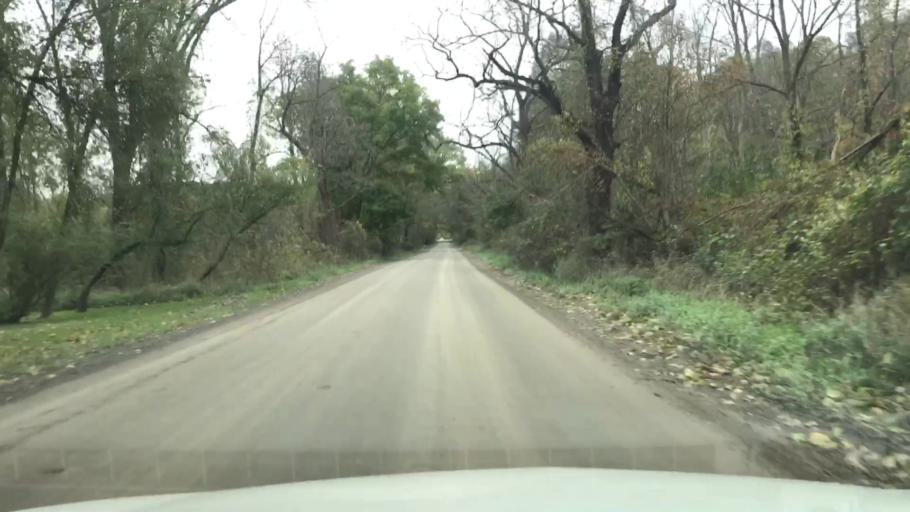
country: US
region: Michigan
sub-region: Oakland County
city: Rochester
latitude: 42.7336
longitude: -83.1143
